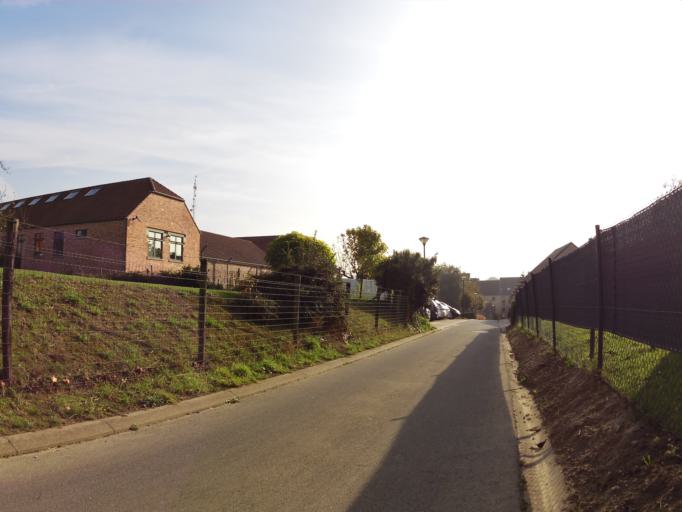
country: BE
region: Flanders
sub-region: Provincie Vlaams-Brabant
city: Wemmel
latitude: 50.9105
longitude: 4.3073
